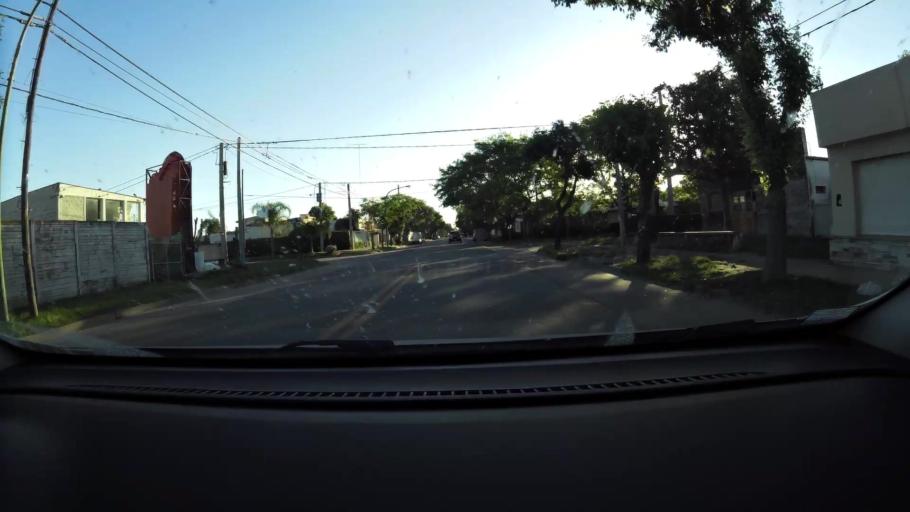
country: AR
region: Cordoba
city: Las Varillas
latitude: -31.8787
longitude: -62.7214
